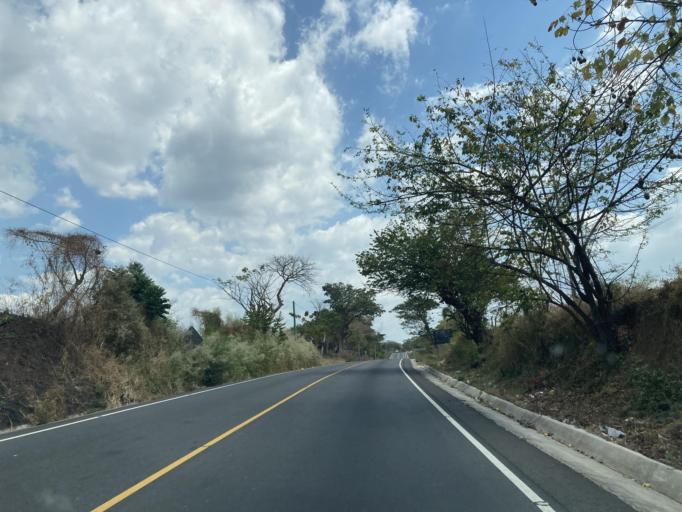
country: GT
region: Santa Rosa
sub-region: Municipio de Taxisco
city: Taxisco
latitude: 14.0635
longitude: -90.4635
